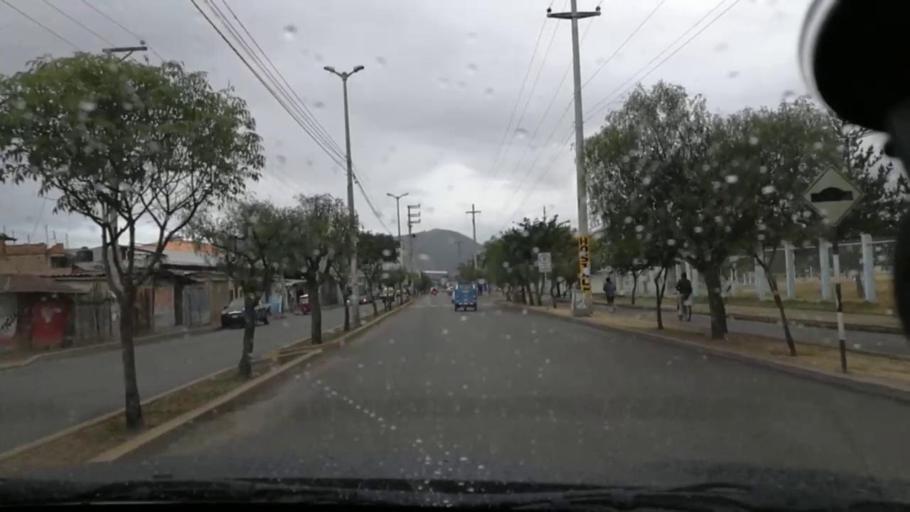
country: PE
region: Cajamarca
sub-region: Provincia de Cajamarca
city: Cajamarca
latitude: -7.1656
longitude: -78.4981
